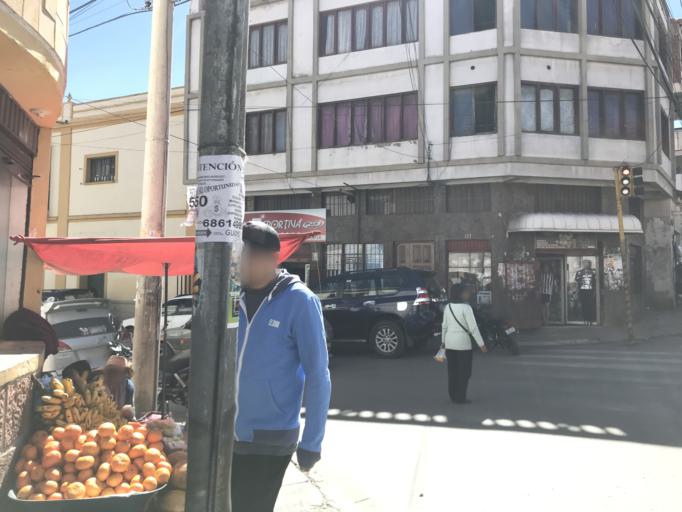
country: BO
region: Chuquisaca
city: Sucre
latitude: -19.0425
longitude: -65.2574
